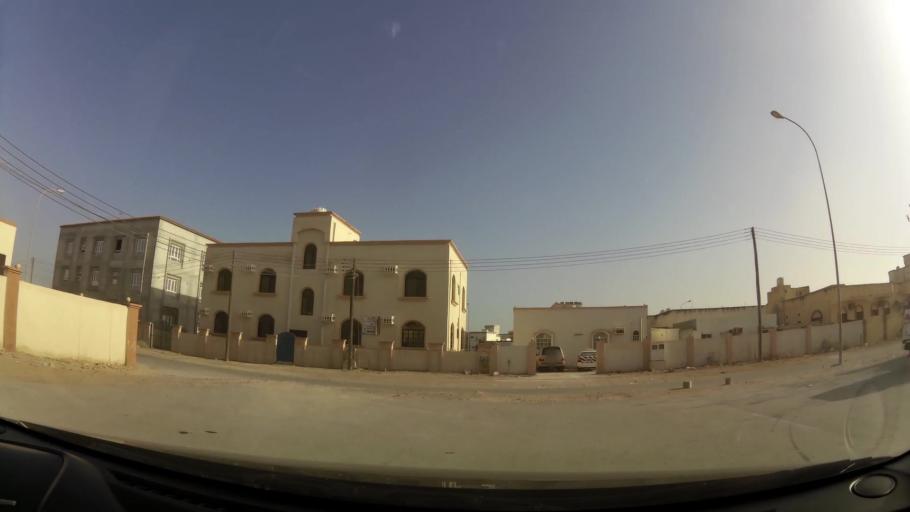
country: OM
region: Zufar
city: Salalah
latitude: 17.0201
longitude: 54.0231
